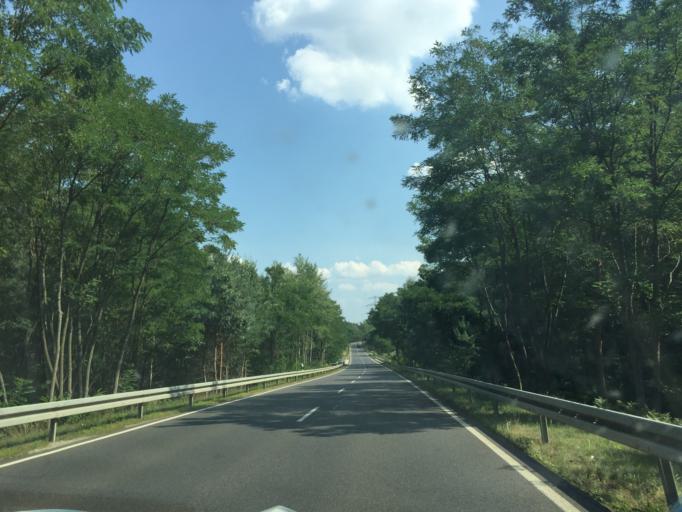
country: DE
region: Saxony
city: Boxberg
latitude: 51.4070
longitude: 14.5465
